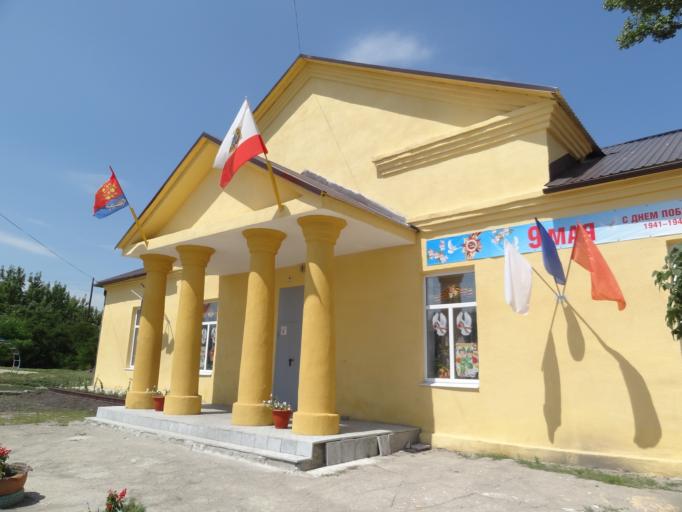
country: RU
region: Saratov
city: Sokolovyy
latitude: 51.4154
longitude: 45.8191
